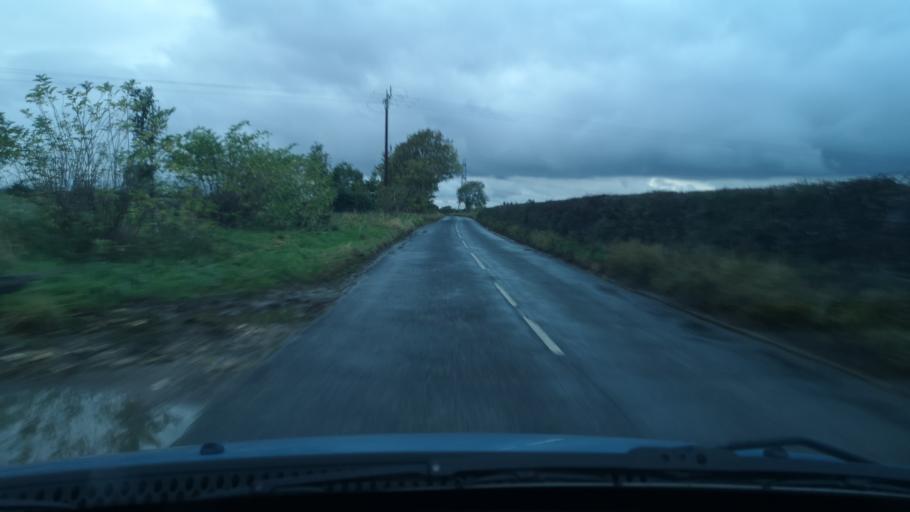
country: GB
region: England
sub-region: Doncaster
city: Norton
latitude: 53.6444
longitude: -1.2263
